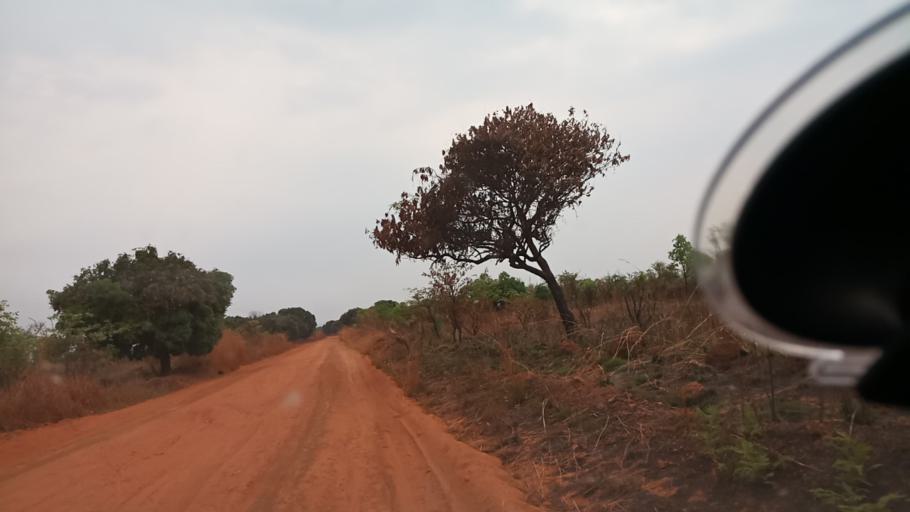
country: ZM
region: Luapula
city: Nchelenge
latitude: -9.1439
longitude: 28.2920
